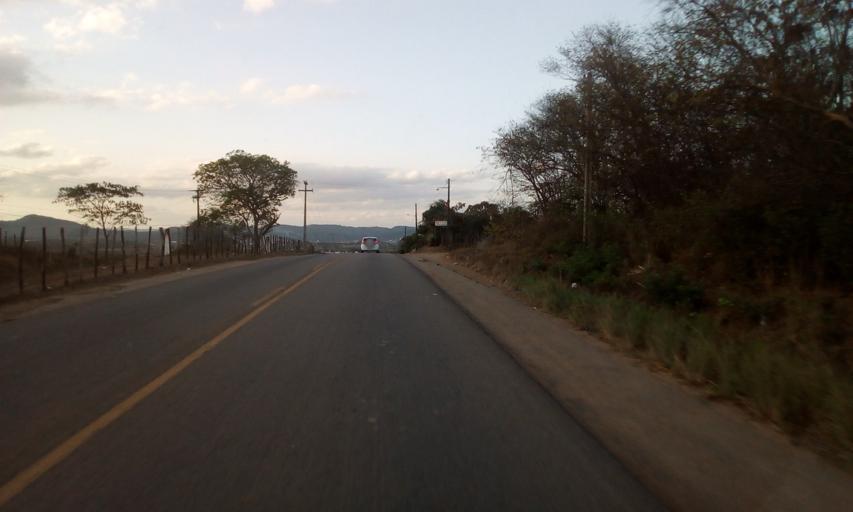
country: BR
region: Paraiba
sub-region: Guarabira
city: Guarabira
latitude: -6.8925
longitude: -35.4650
